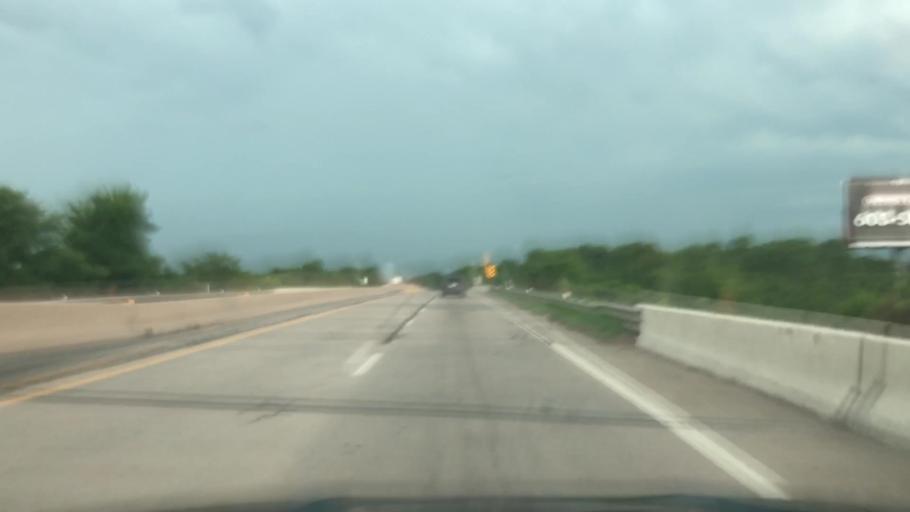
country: US
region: Oklahoma
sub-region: Rogers County
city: Claremore
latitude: 36.2967
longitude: -95.6014
